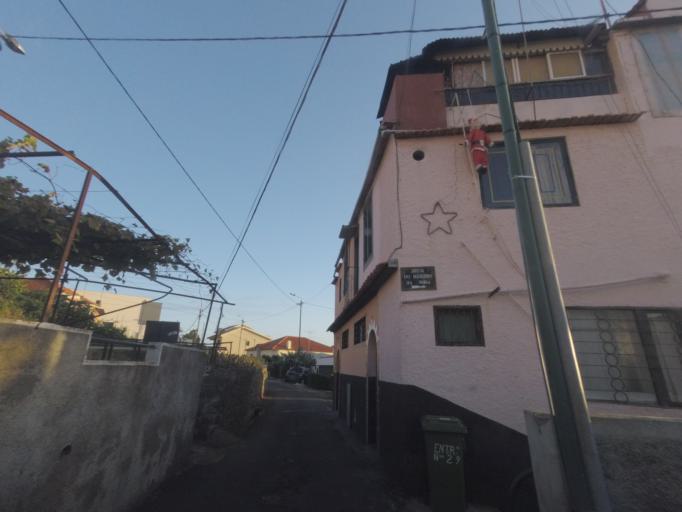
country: PT
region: Madeira
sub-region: Funchal
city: Nossa Senhora do Monte
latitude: 32.6565
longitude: -16.8908
